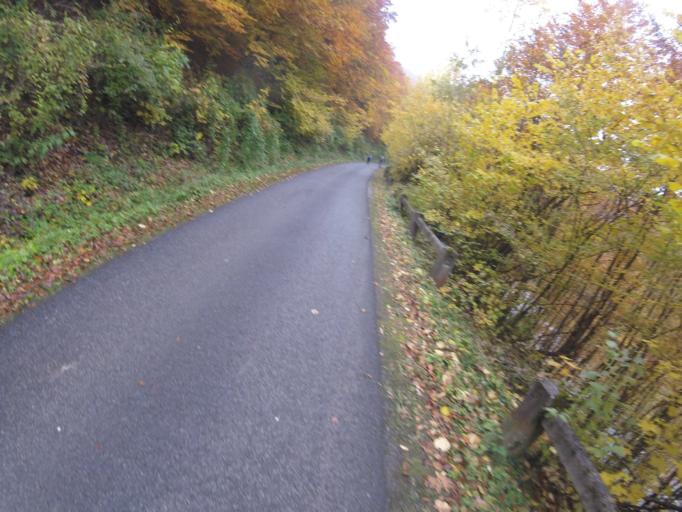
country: HU
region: Borsod-Abauj-Zemplen
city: Putnok
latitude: 48.2099
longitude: 20.4567
